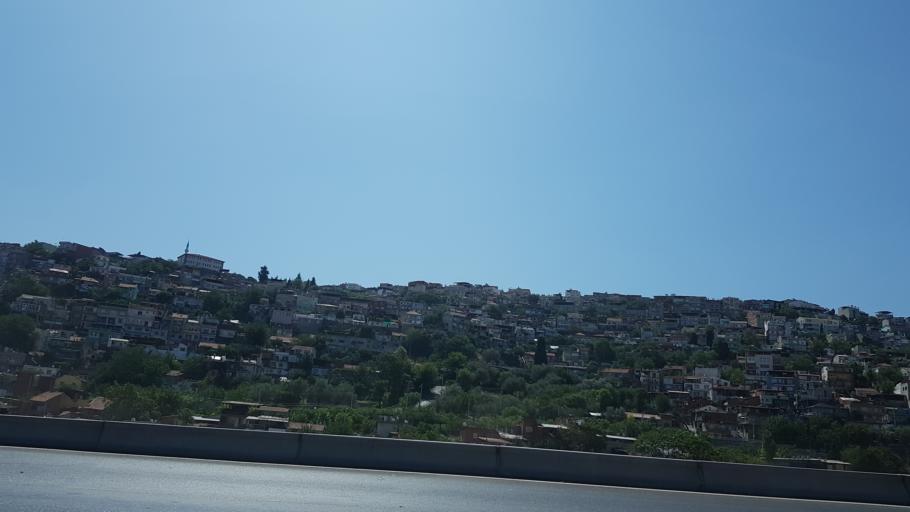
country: TR
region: Izmir
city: Izmir
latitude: 38.4102
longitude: 27.1545
